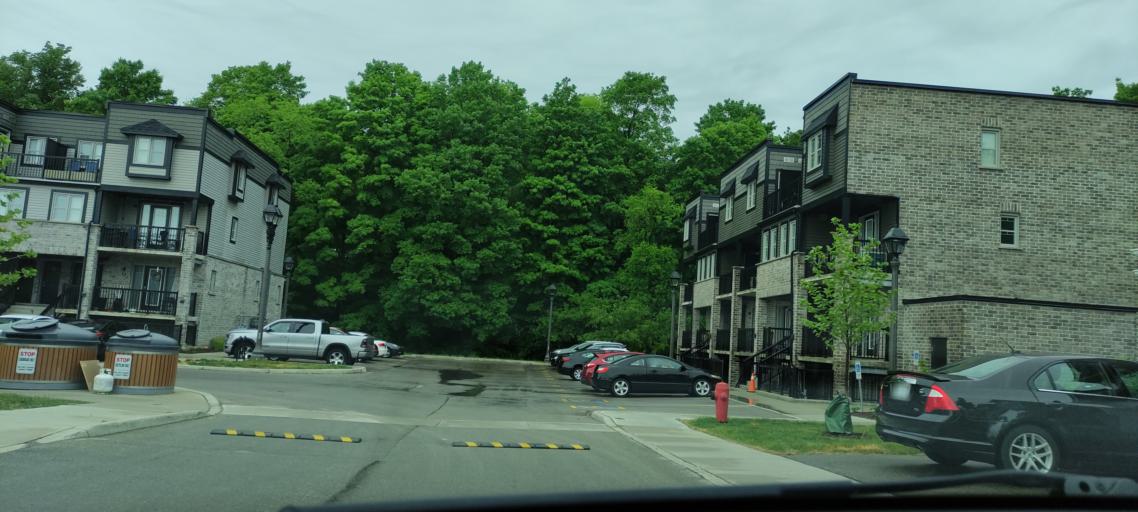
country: CA
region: Ontario
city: Kitchener
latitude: 43.4059
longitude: -80.5300
